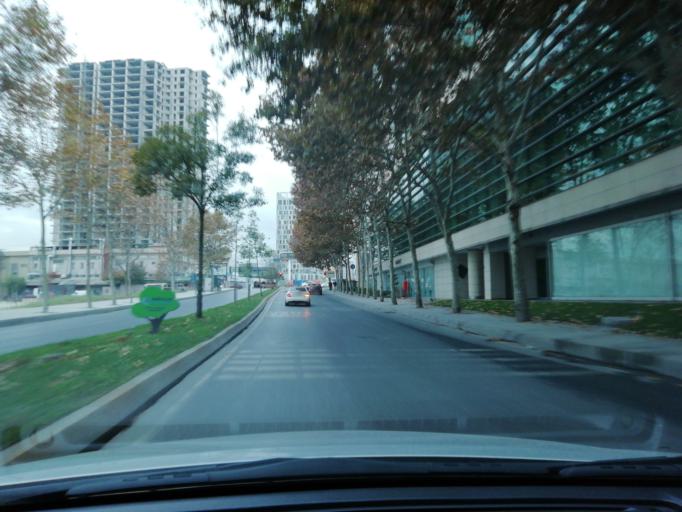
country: TR
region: Istanbul
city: Mahmutbey
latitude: 41.0238
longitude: 28.8187
